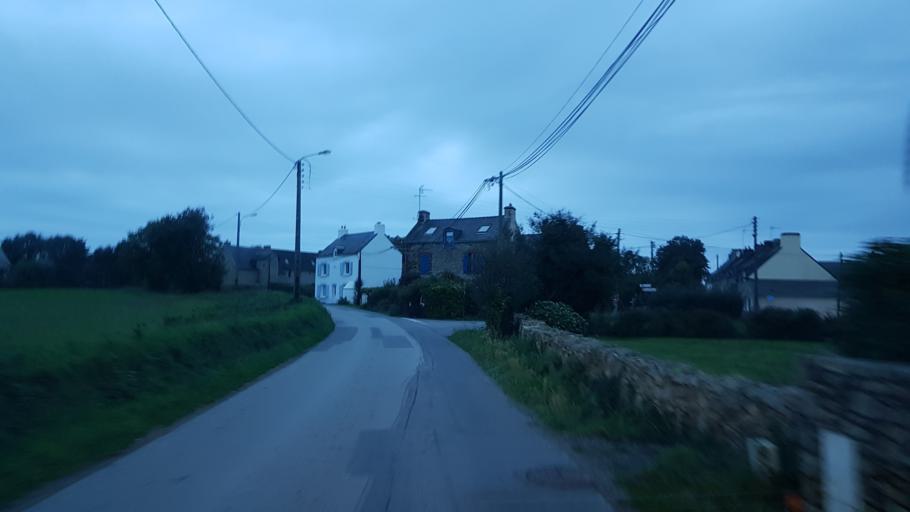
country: FR
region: Brittany
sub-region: Departement du Morbihan
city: Sarzeau
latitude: 47.5429
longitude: -2.7892
